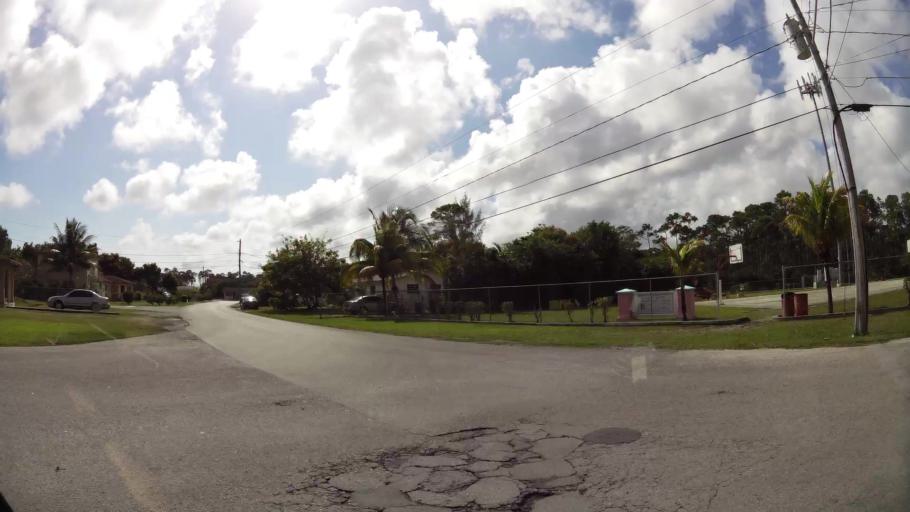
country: BS
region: Freeport
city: Lucaya
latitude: 26.5321
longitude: -78.6749
